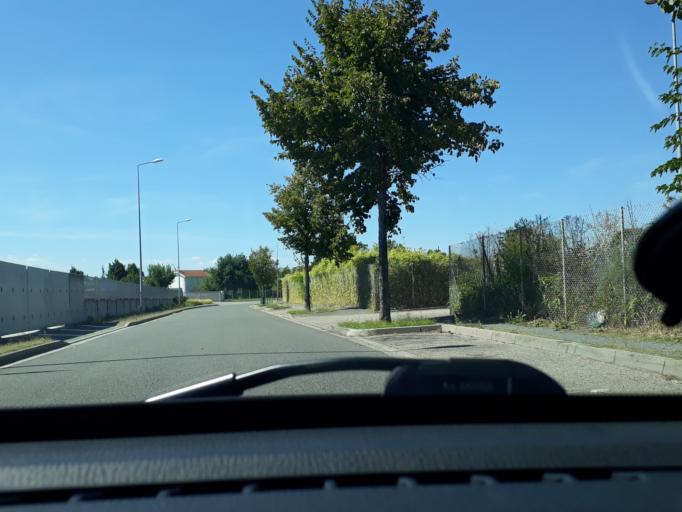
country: FR
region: Rhone-Alpes
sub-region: Departement du Rhone
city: Saint-Priest
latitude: 45.6958
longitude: 4.9204
